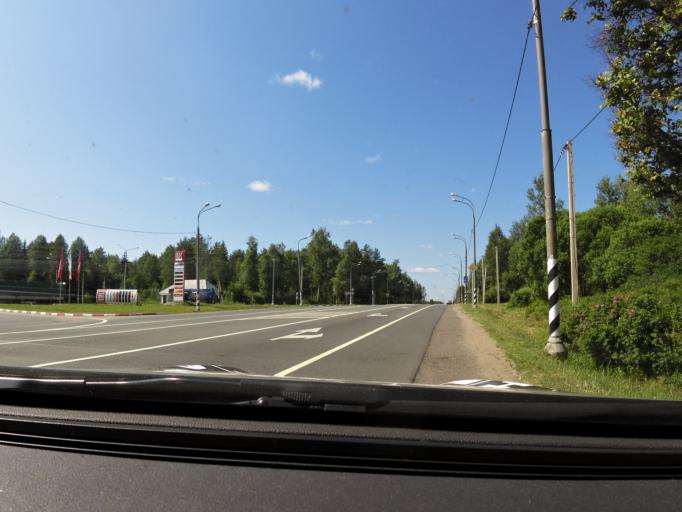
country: RU
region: Novgorod
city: Kresttsy
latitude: 58.1758
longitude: 32.6999
